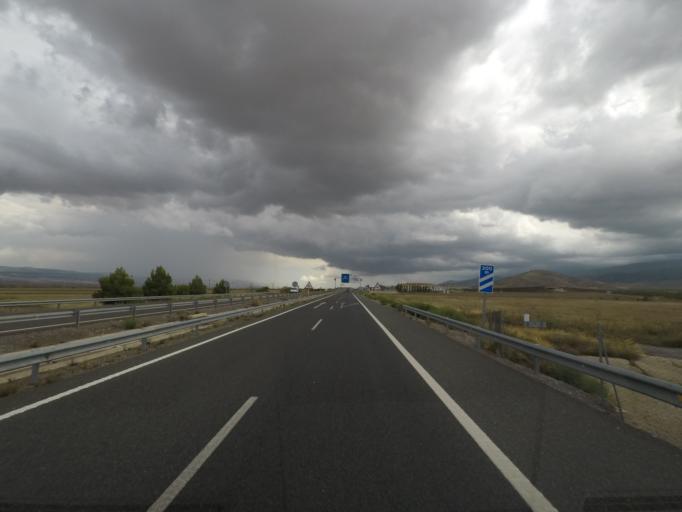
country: ES
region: Andalusia
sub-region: Provincia de Granada
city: Ferreira
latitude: 37.2080
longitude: -3.0537
